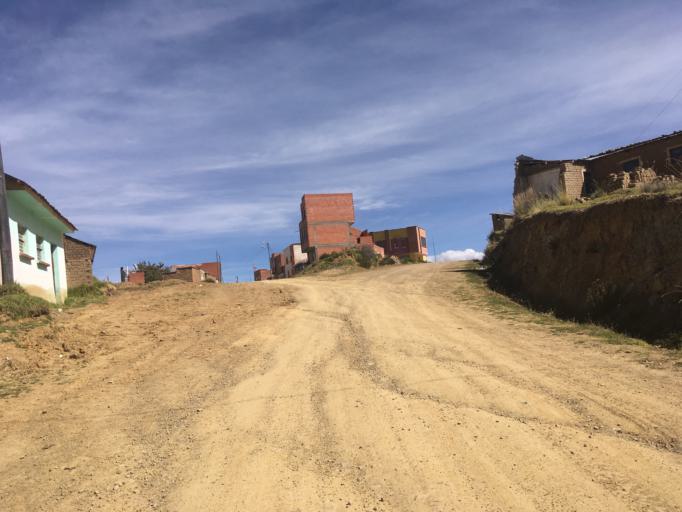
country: BO
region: La Paz
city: San Pedro
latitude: -16.2620
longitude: -68.8797
